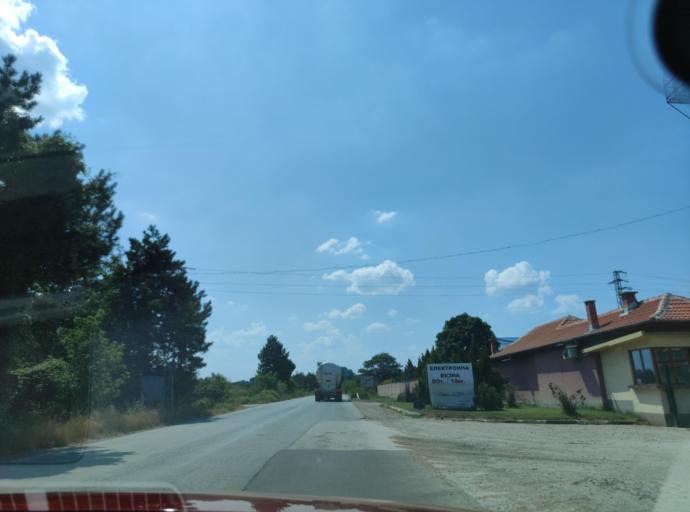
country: BG
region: Pleven
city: Iskur
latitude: 43.4534
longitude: 24.2512
